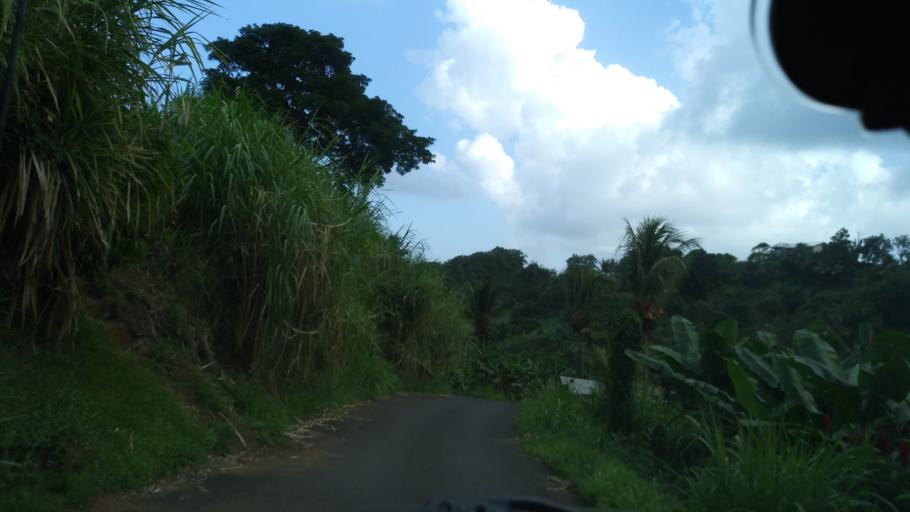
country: VC
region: Charlotte
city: Byera Village
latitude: 13.2319
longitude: -61.1349
